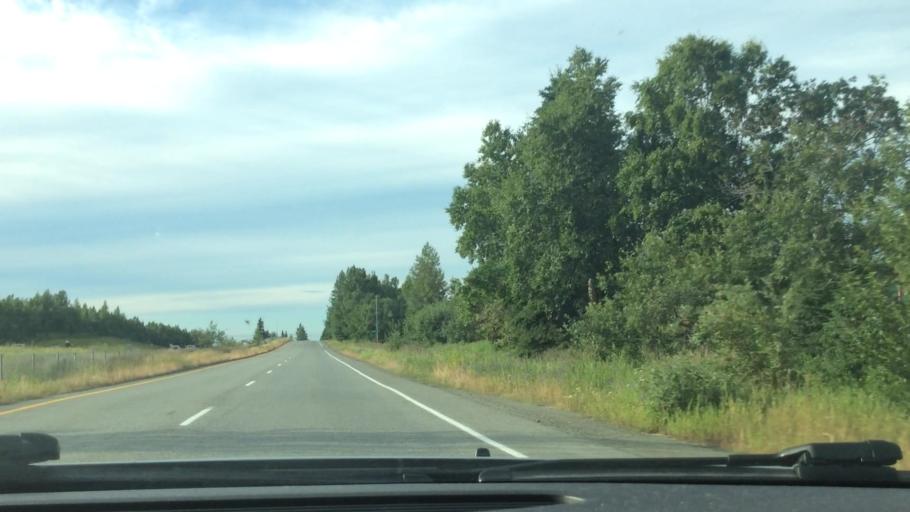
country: US
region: Alaska
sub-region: Anchorage Municipality
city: Anchorage
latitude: 61.1281
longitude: -149.8557
